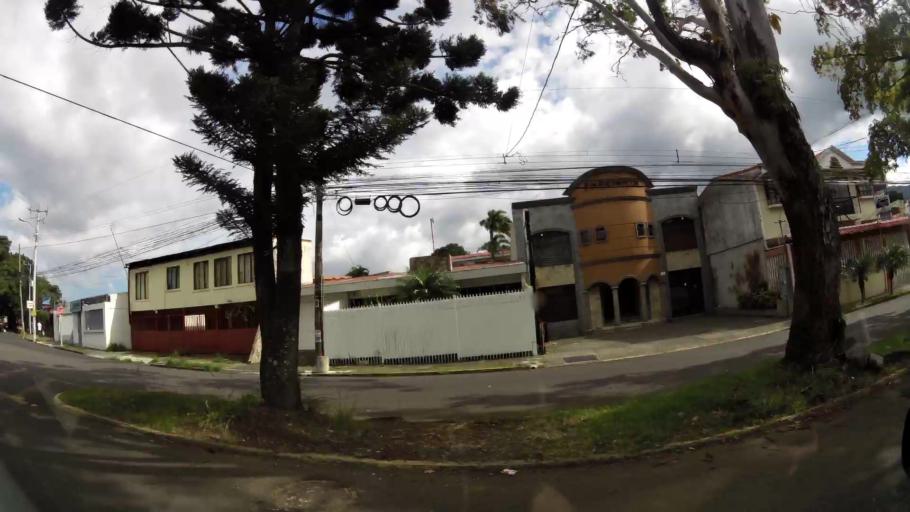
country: CR
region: San Jose
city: San Rafael
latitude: 9.9470
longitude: -84.1292
